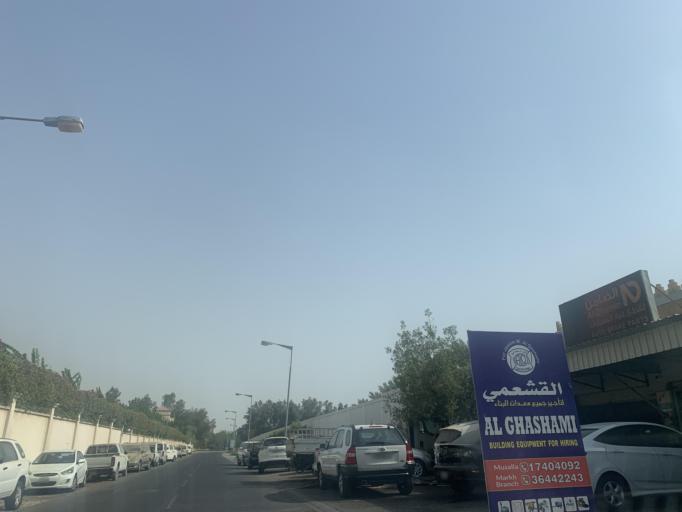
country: BH
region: Manama
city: Jidd Hafs
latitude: 26.2152
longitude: 50.4737
